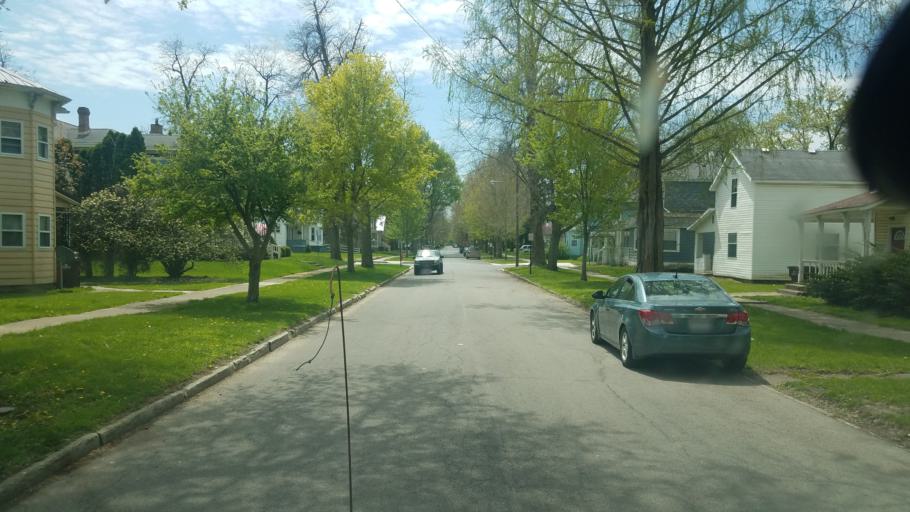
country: US
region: Ohio
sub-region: Hardin County
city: Ada
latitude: 40.7674
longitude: -83.8216
